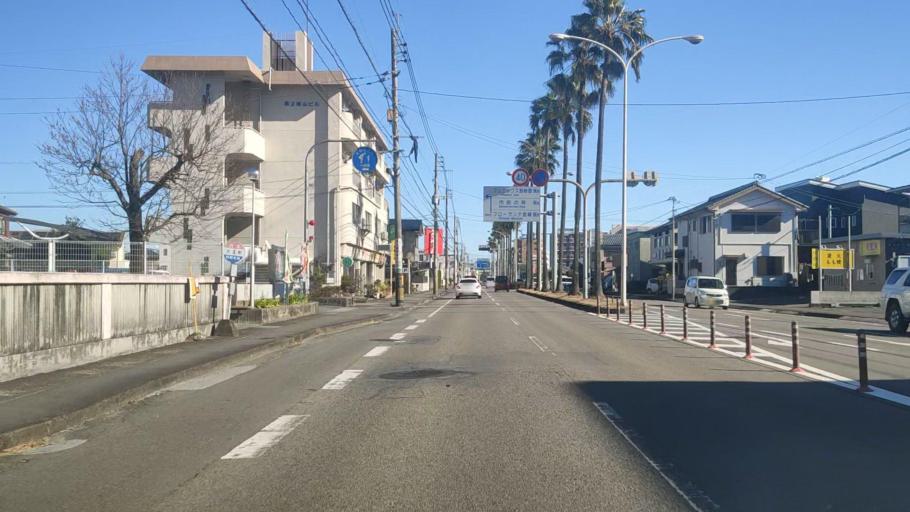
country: JP
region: Miyazaki
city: Miyazaki-shi
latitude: 31.9076
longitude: 131.4432
